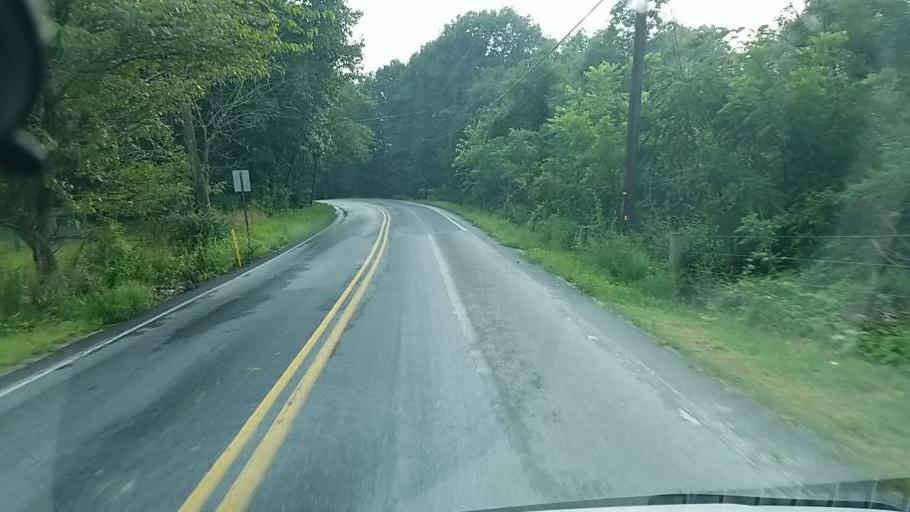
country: US
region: Pennsylvania
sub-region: Cumberland County
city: Newville
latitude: 40.1916
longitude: -77.5126
